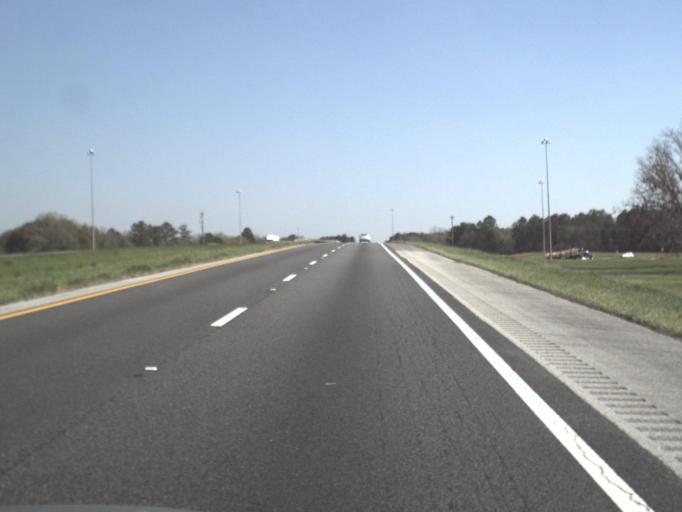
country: US
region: Florida
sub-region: Jackson County
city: Sneads
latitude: 30.6583
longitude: -85.0405
